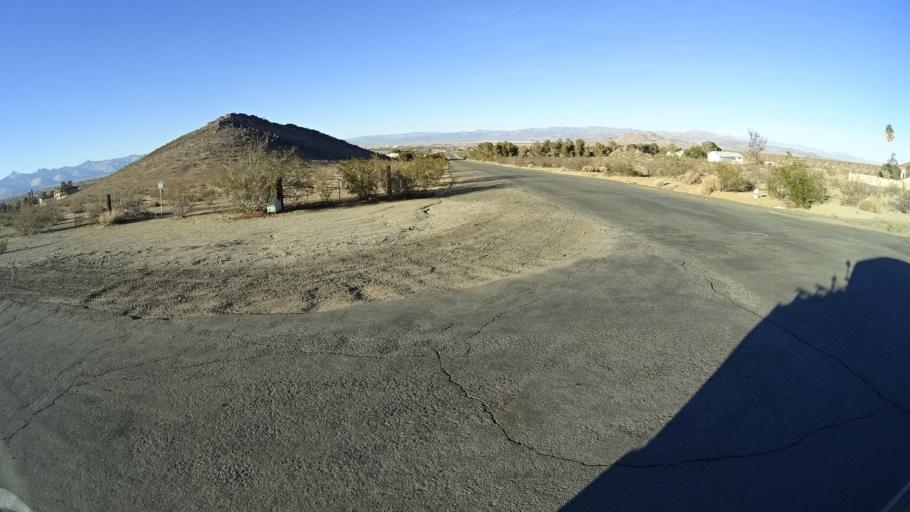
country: US
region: California
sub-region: Kern County
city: Ridgecrest
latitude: 35.5786
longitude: -117.6478
